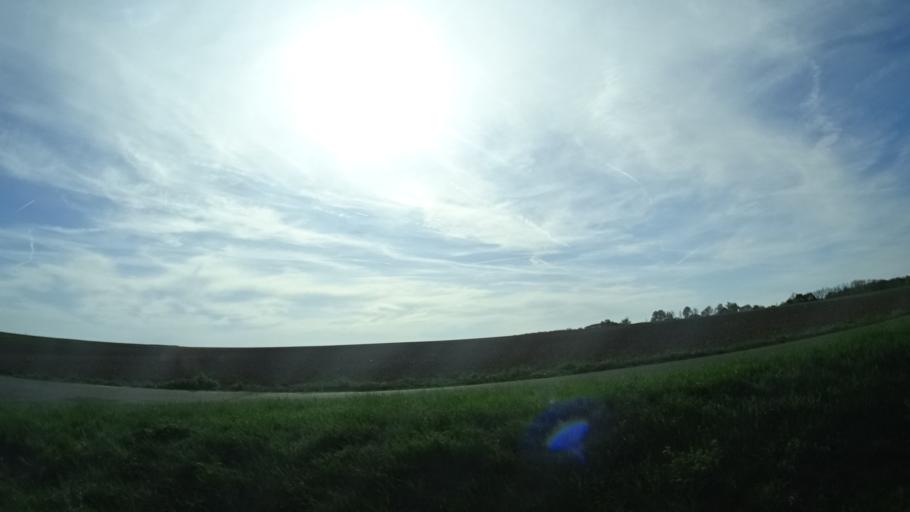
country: DE
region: Bavaria
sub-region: Regierungsbezirk Unterfranken
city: Volkach
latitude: 49.8864
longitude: 10.2278
